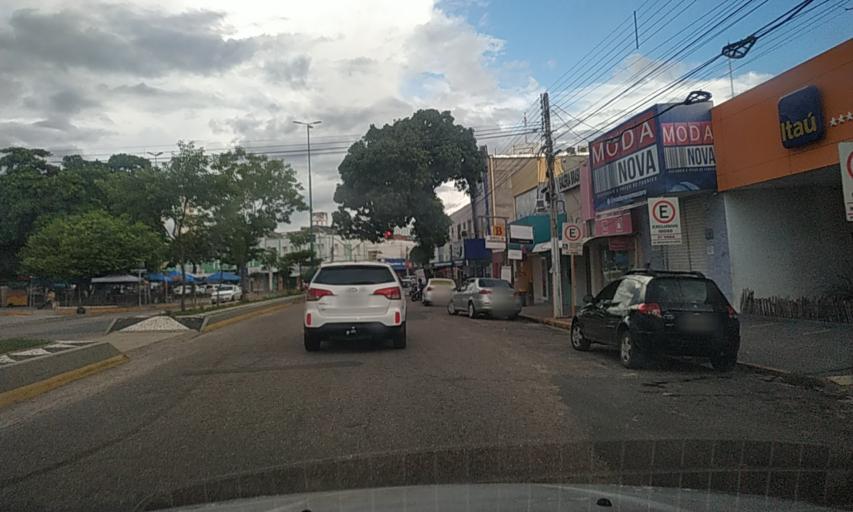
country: BR
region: Rio Grande do Norte
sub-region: Mossoro
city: Mossoro
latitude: -5.1916
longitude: -37.3430
